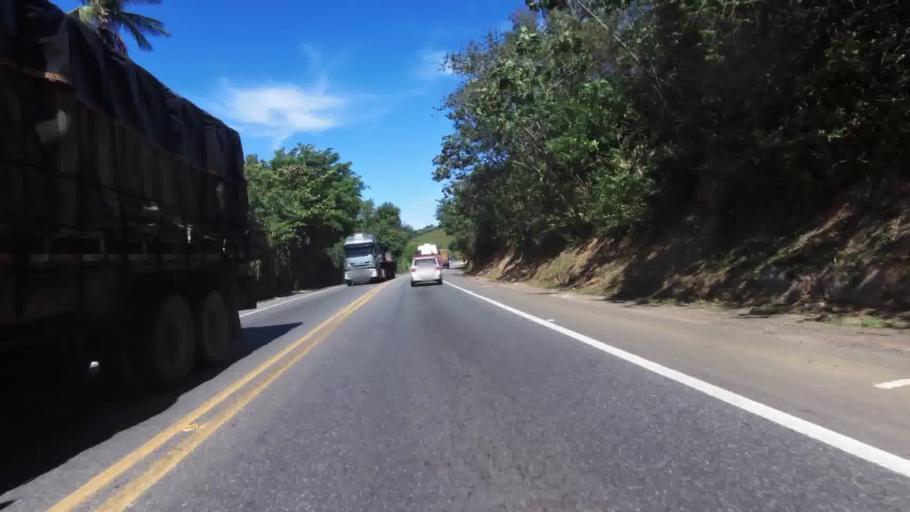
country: BR
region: Espirito Santo
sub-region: Iconha
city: Iconha
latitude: -20.8361
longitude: -40.8671
